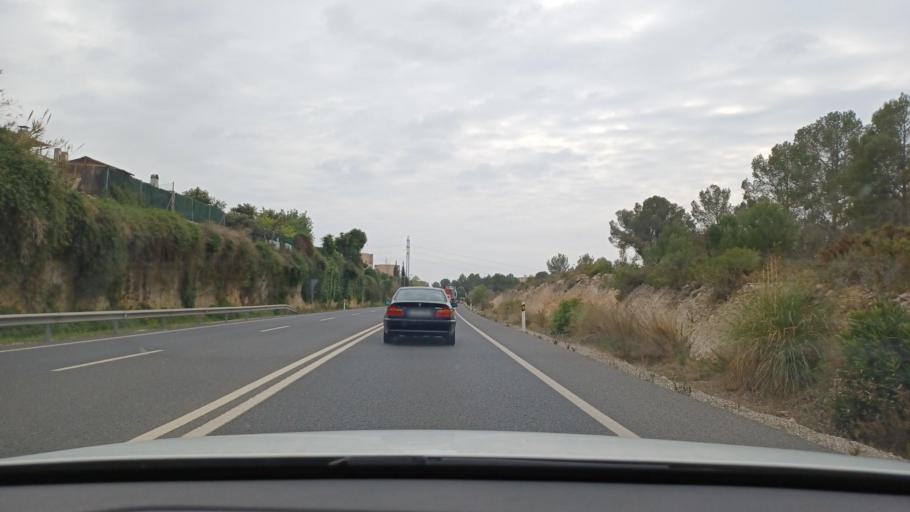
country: ES
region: Catalonia
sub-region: Provincia de Tarragona
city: els Pallaresos
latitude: 41.1622
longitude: 1.2399
